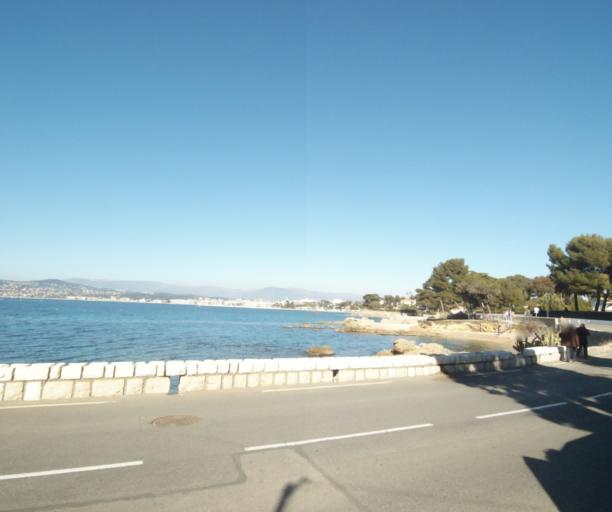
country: FR
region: Provence-Alpes-Cote d'Azur
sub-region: Departement des Alpes-Maritimes
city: Antibes
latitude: 43.5521
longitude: 7.1220
